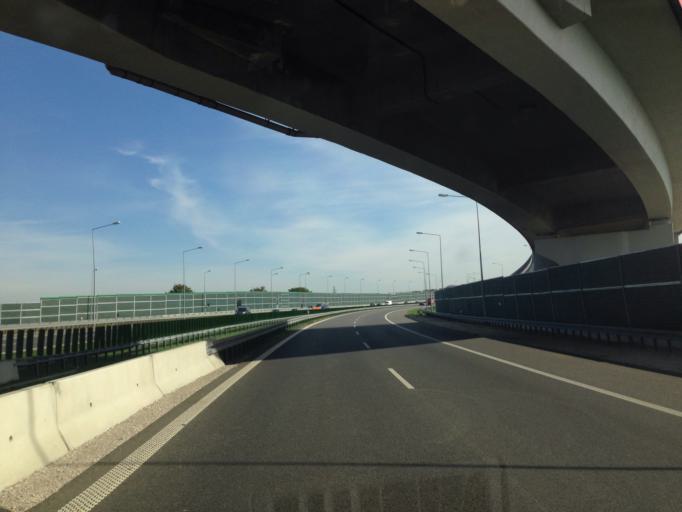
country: PL
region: Masovian Voivodeship
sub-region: Powiat pruszkowski
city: Piastow
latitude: 52.1999
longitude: 20.8427
